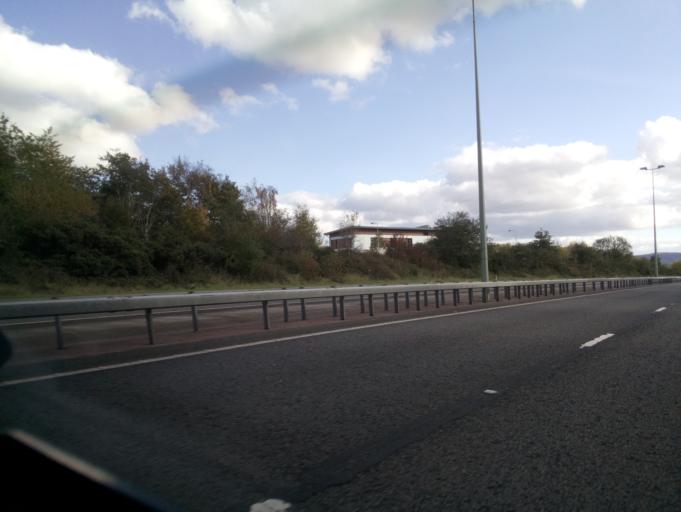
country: GB
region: Wales
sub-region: Merthyr Tydfil County Borough
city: Merthyr Tydfil
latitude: 51.7463
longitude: -3.3917
